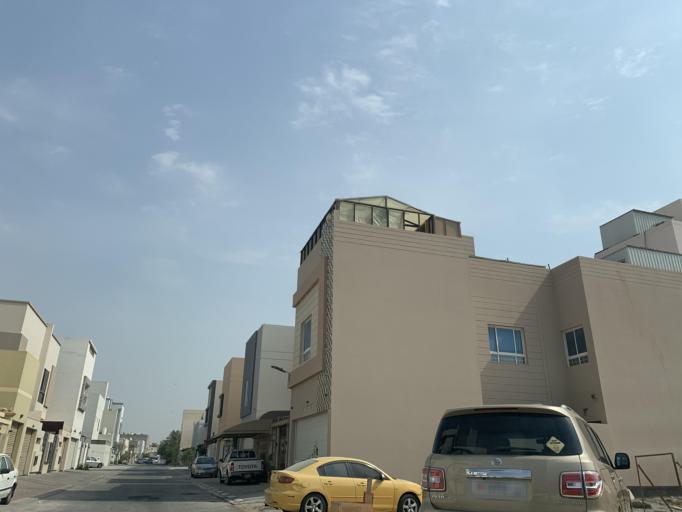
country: BH
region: Manama
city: Jidd Hafs
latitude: 26.2133
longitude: 50.4867
